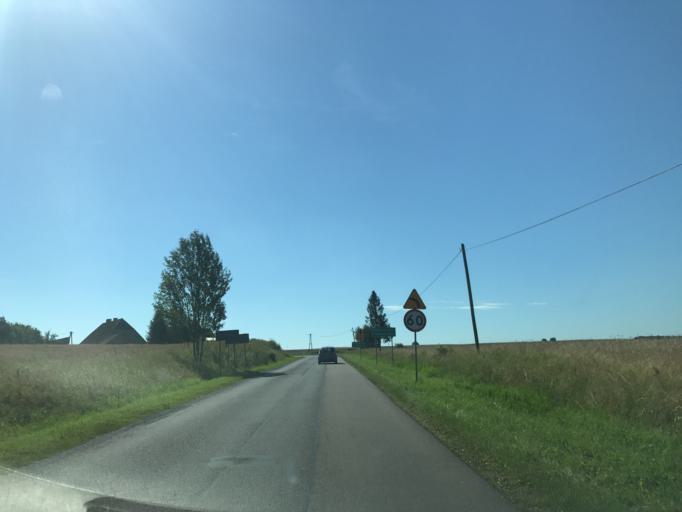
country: PL
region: Pomeranian Voivodeship
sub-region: Powiat bytowski
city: Czarna Dabrowka
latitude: 54.3682
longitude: 17.5034
